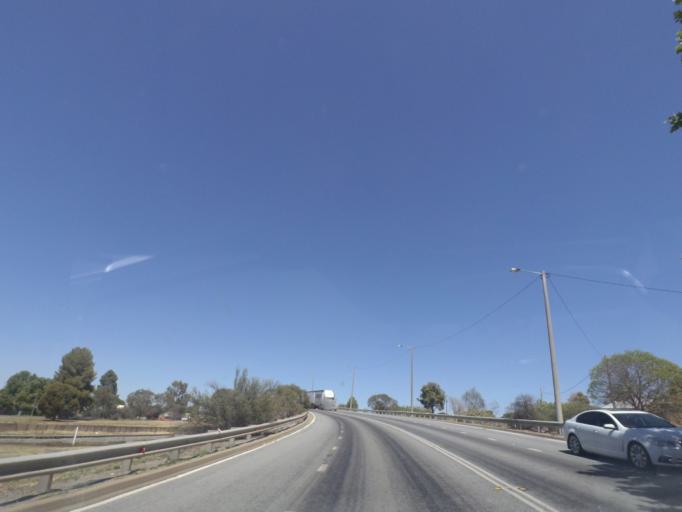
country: AU
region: New South Wales
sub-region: Narrandera
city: Narrandera
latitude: -34.7400
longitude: 146.5608
